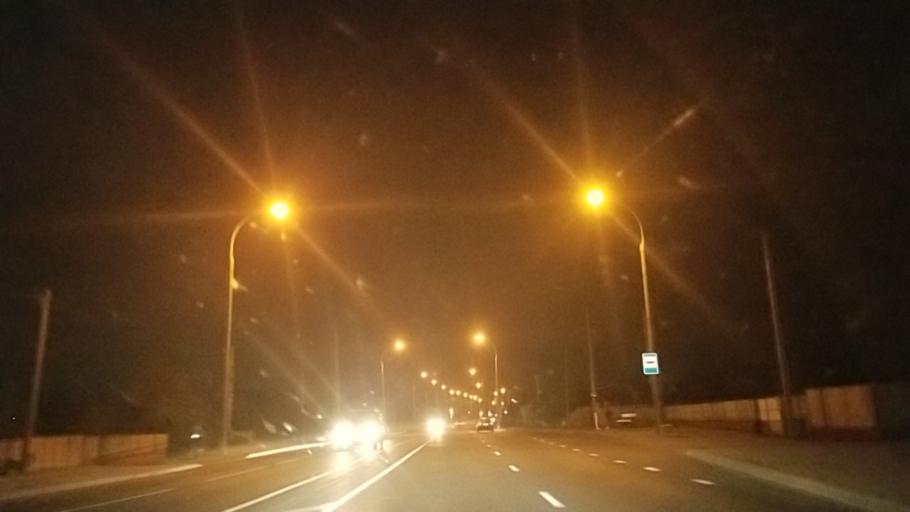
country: BY
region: Brest
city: Brest
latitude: 52.0662
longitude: 23.7399
